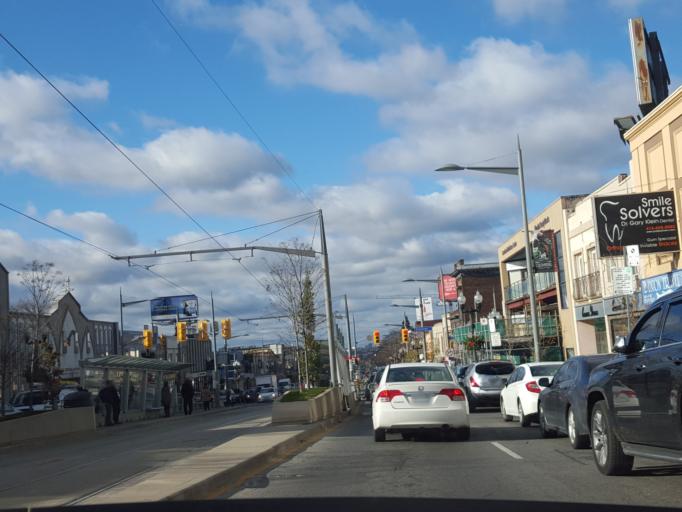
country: CA
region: Ontario
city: Toronto
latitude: 43.6773
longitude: -79.4465
